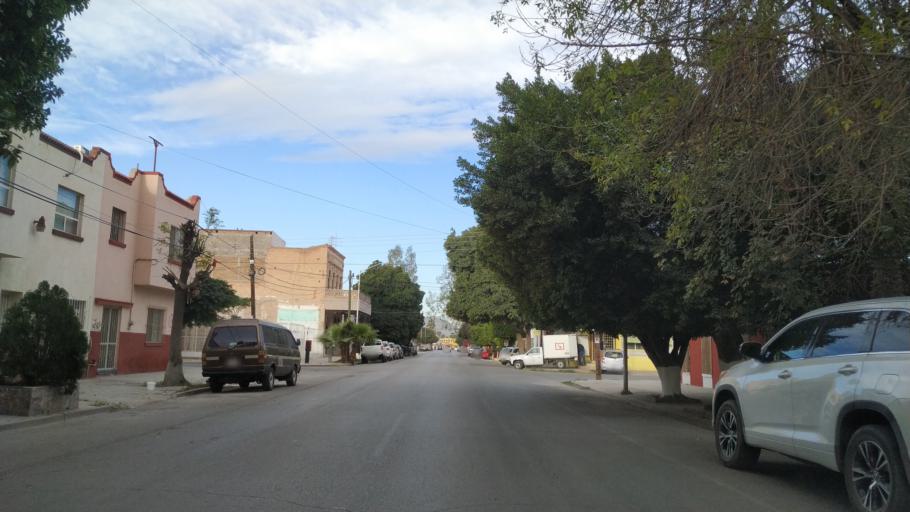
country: MX
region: Coahuila
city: Torreon
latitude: 25.5441
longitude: -103.4512
